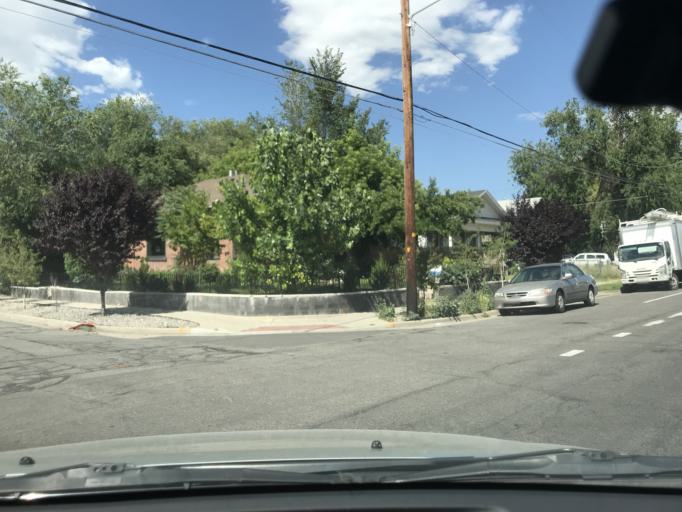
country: US
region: Utah
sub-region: Salt Lake County
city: Salt Lake City
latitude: 40.7607
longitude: -111.9210
